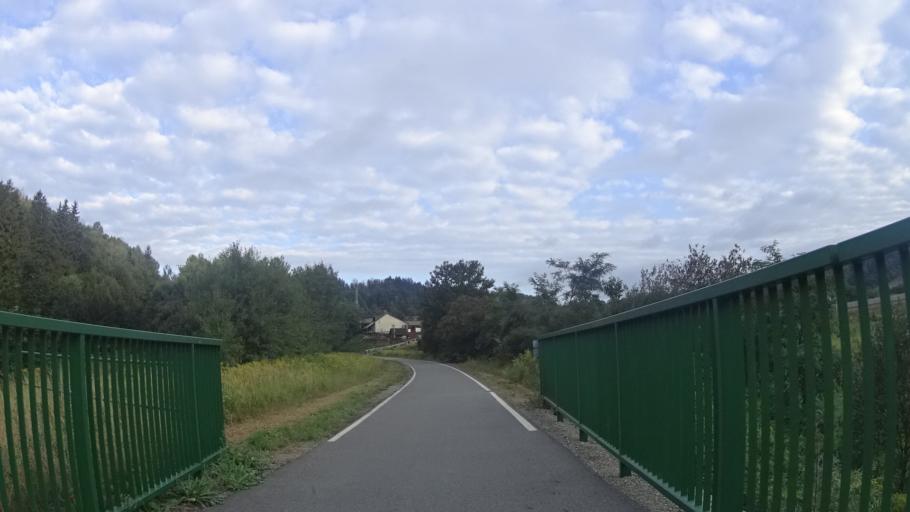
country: CZ
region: Olomoucky
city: Zabreh
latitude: 49.8623
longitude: 16.8194
